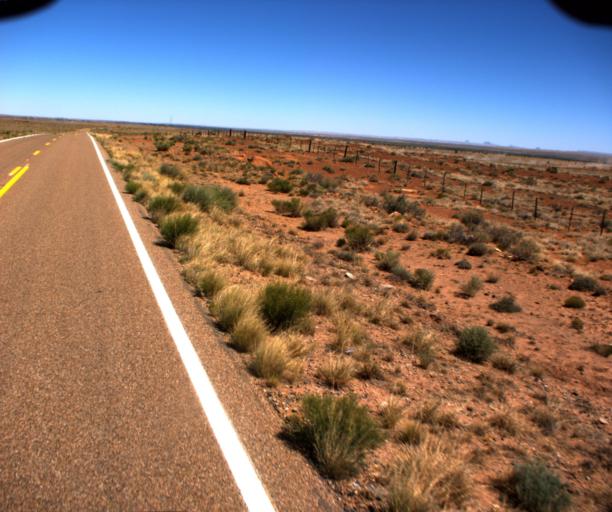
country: US
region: Arizona
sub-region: Navajo County
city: Winslow
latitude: 34.9352
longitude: -110.6407
